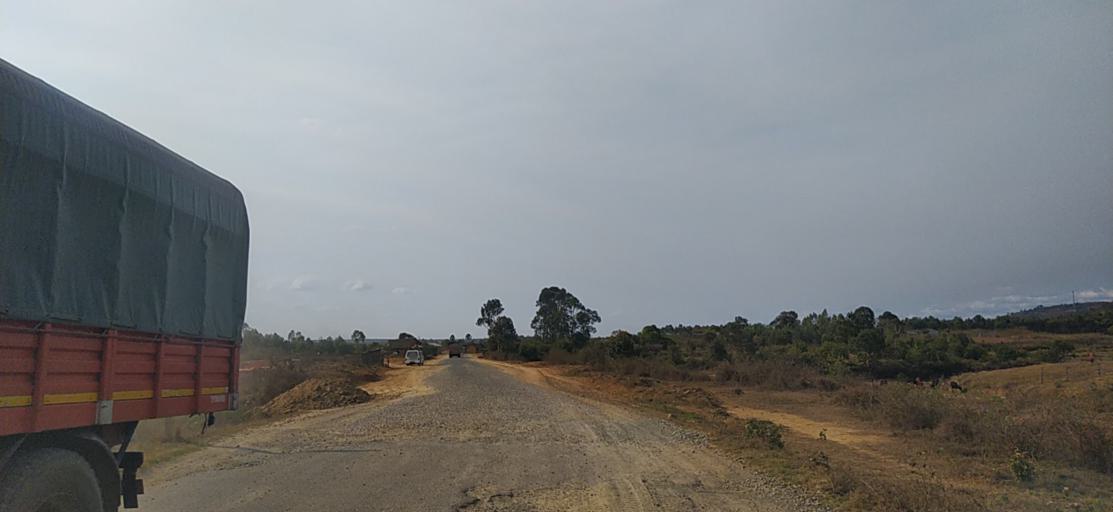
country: MG
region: Alaotra Mangoro
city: Moramanga
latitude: -18.6654
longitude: 48.2746
